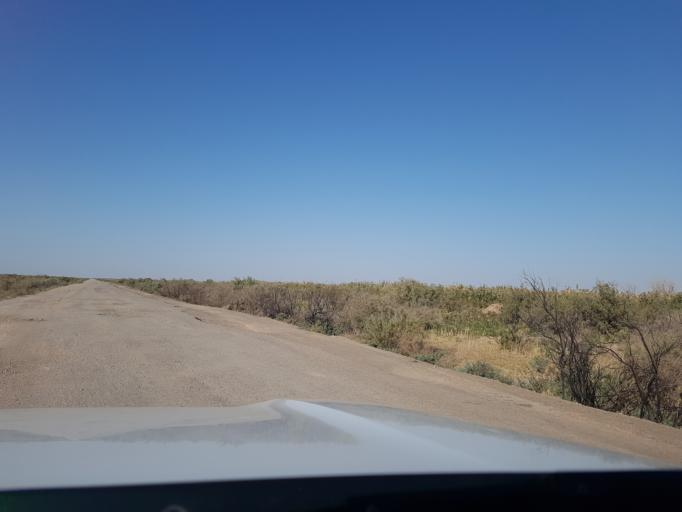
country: IR
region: Razavi Khorasan
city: Sarakhs
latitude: 36.9590
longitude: 61.3817
